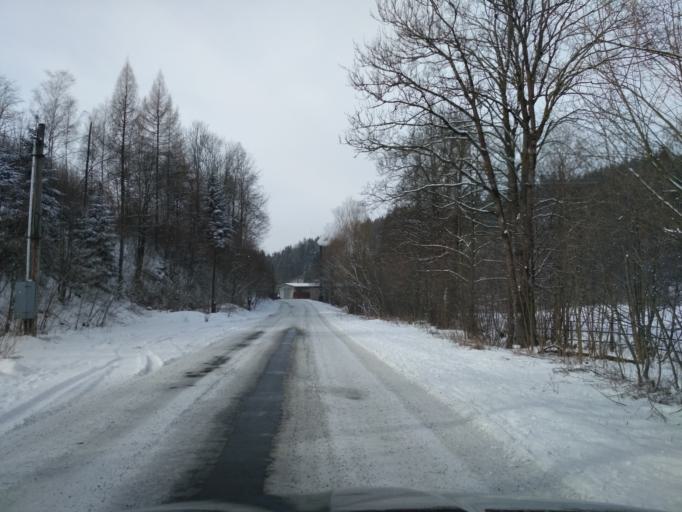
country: CZ
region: Zlin
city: Valasska Bystrice
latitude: 49.4094
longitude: 18.1235
